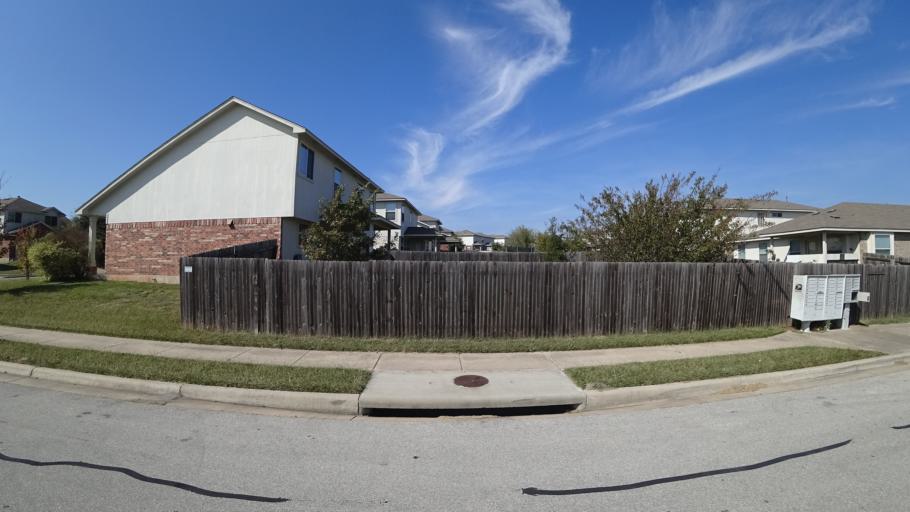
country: US
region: Texas
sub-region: Travis County
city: Pflugerville
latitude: 30.4253
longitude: -97.6358
